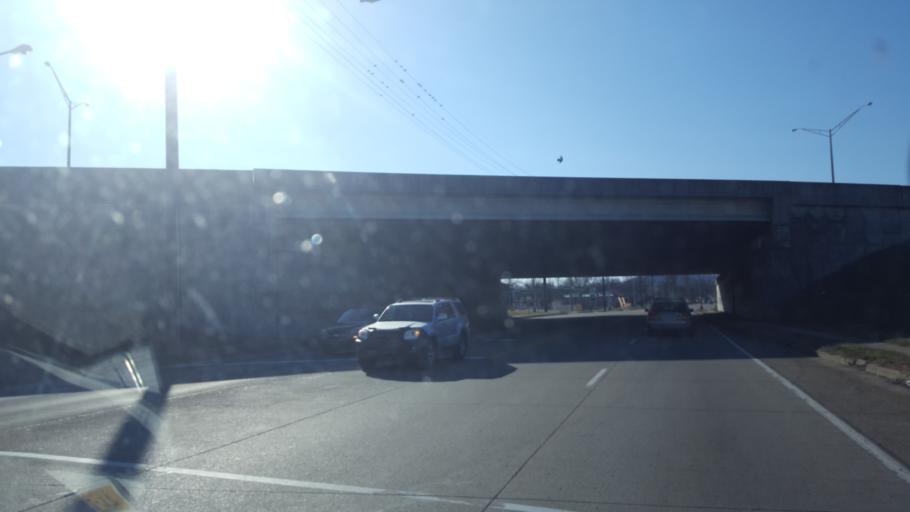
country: US
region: Kentucky
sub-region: Jefferson County
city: Shively
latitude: 38.1894
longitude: -85.7835
